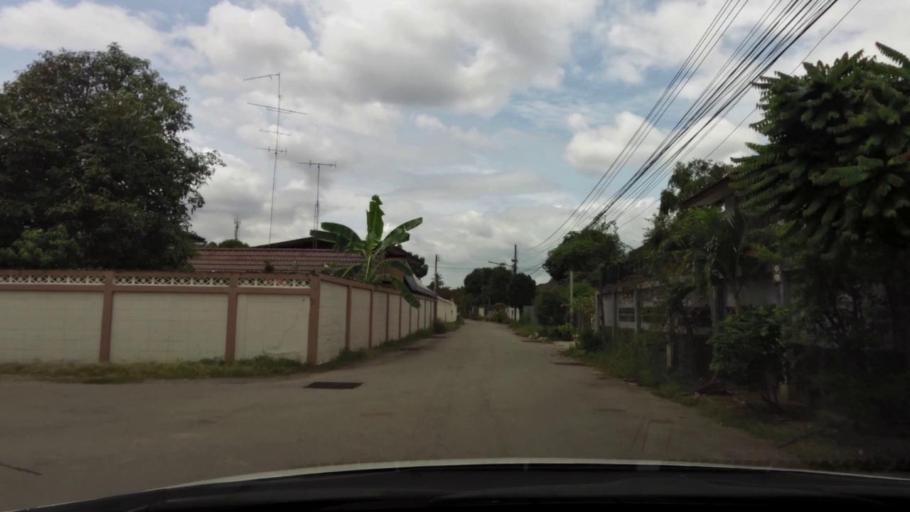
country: TH
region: Ratchaburi
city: Ratchaburi
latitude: 13.5346
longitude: 99.8253
